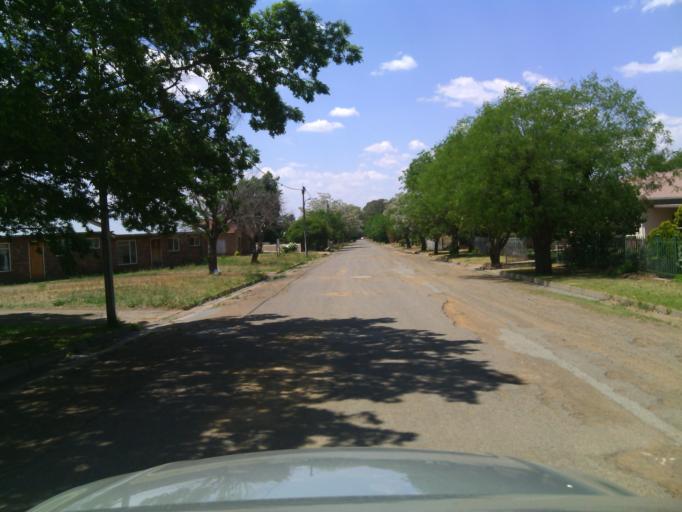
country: ZA
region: Orange Free State
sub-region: Xhariep District Municipality
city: Dewetsdorp
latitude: -29.5805
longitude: 26.6648
